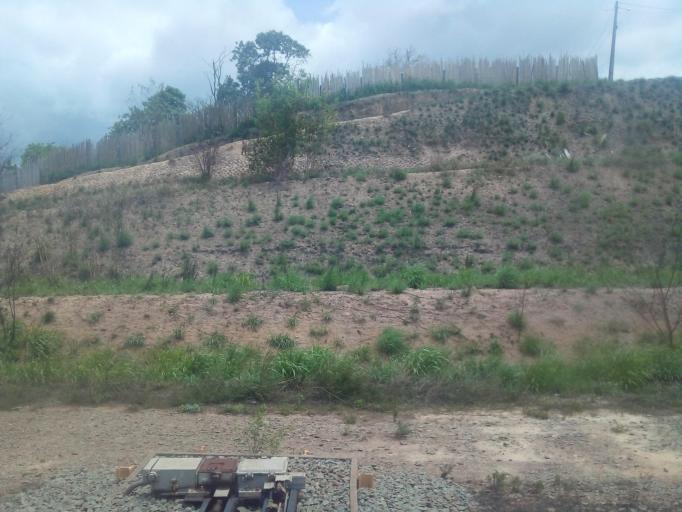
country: BR
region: Maranhao
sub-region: Santa Ines
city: Santa Ines
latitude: -3.6707
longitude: -45.8451
